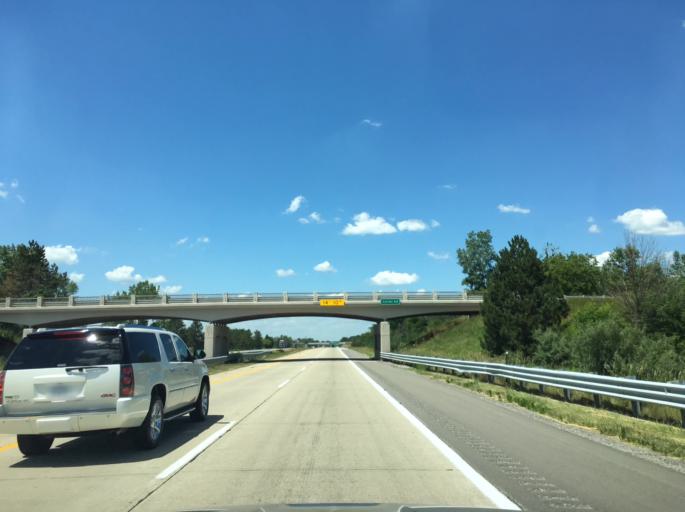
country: US
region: Michigan
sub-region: Bay County
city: Auburn
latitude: 43.5976
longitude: -84.1280
